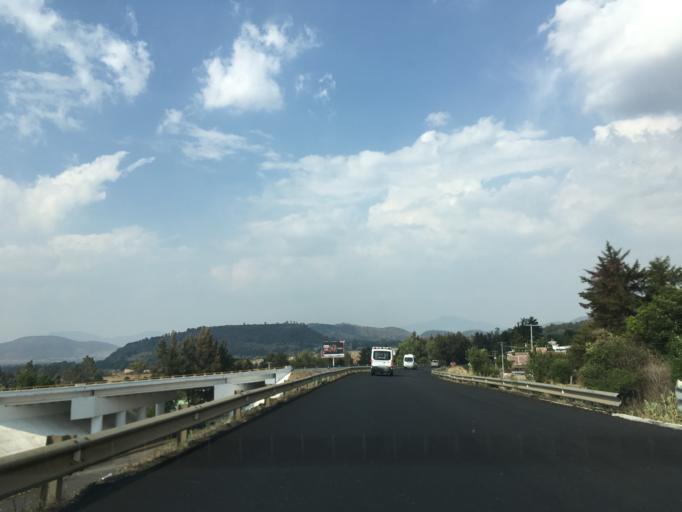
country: MX
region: Michoacan
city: Patzcuaro
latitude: 19.5295
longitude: -101.5622
